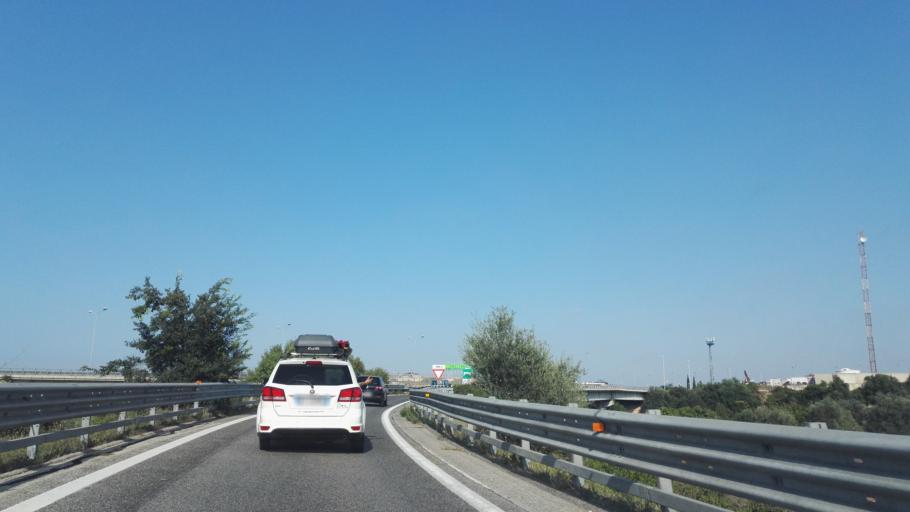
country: IT
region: Apulia
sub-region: Provincia di Bari
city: Modugno
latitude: 41.0975
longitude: 16.8241
